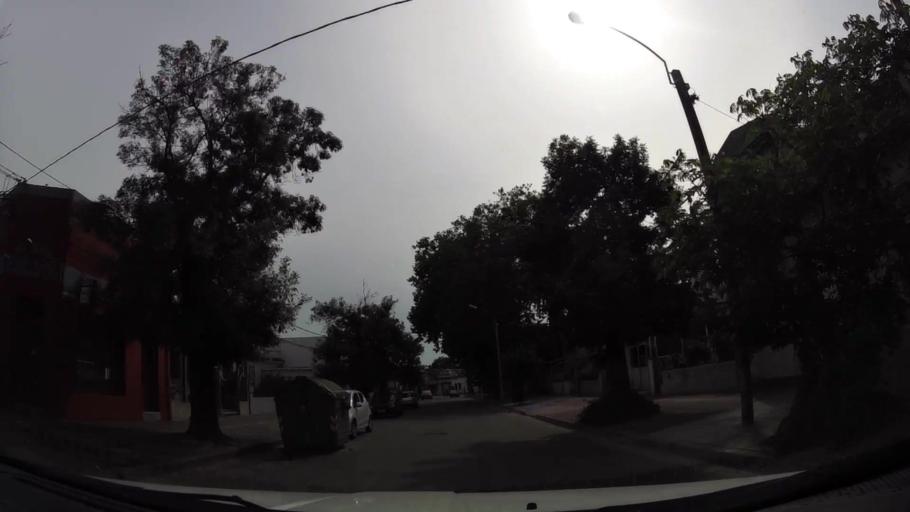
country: UY
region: Montevideo
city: Montevideo
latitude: -34.8685
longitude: -56.2120
